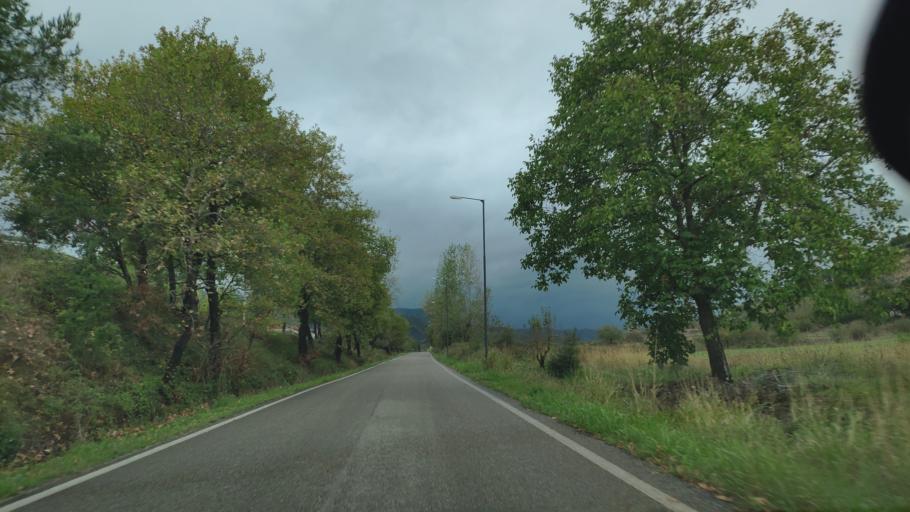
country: GR
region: West Greece
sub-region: Nomos Aitolias kai Akarnanias
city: Krikellos
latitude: 38.9751
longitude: 21.3290
